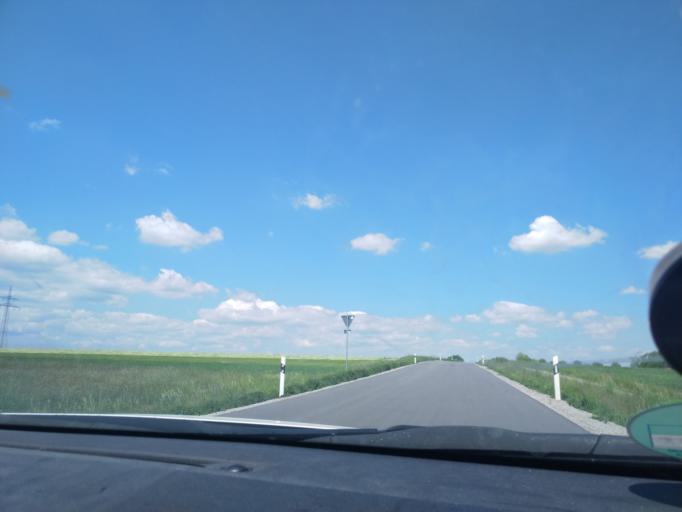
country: DE
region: Baden-Wuerttemberg
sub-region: Freiburg Region
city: Dornhan
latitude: 48.3311
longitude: 8.4689
